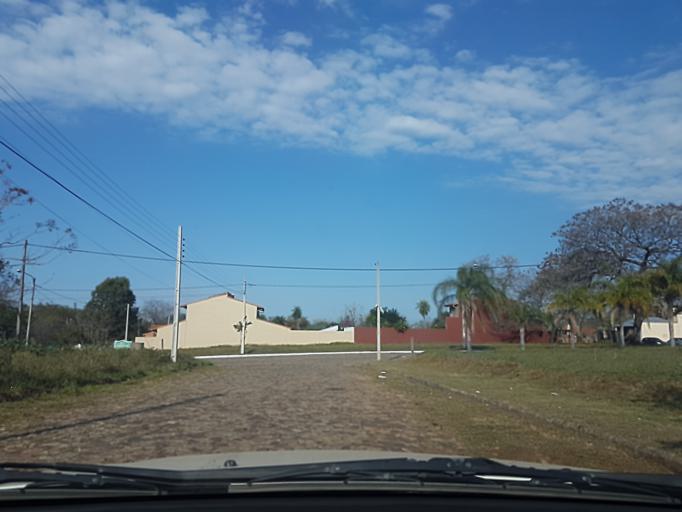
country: PY
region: Central
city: Colonia Mariano Roque Alonso
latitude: -25.2449
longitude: -57.5382
